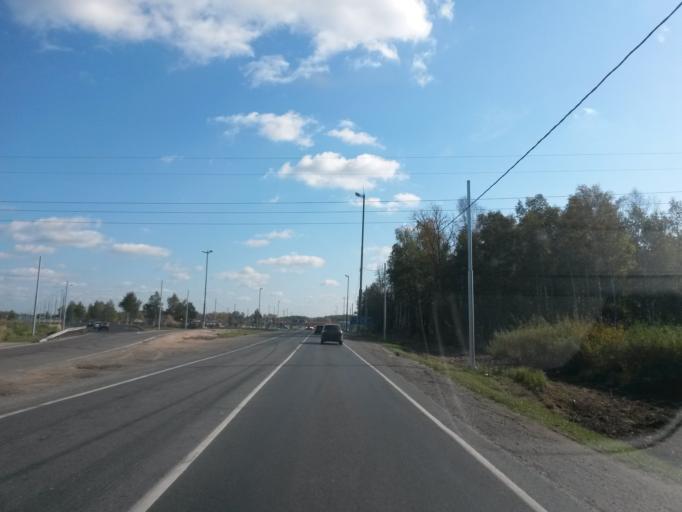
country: RU
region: Moskovskaya
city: L'vovskiy
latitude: 55.3321
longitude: 37.5564
